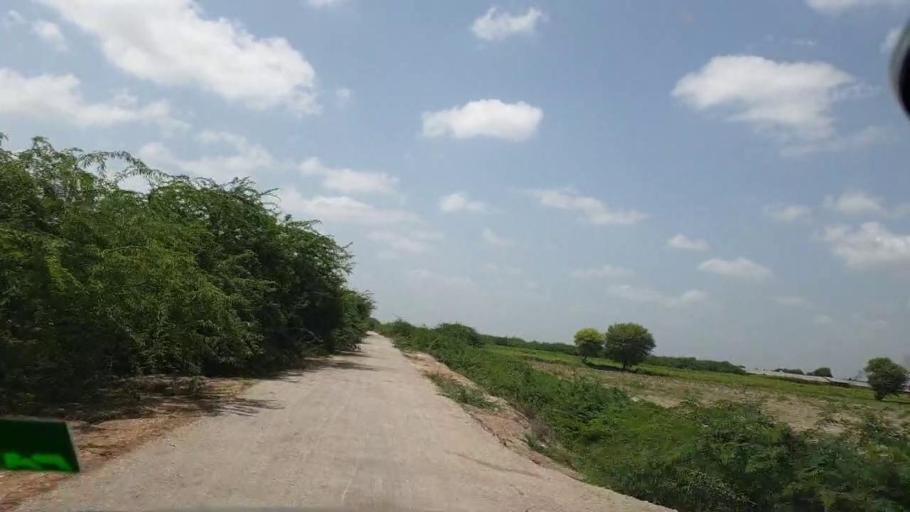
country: PK
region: Sindh
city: Kadhan
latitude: 24.5517
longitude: 69.2004
